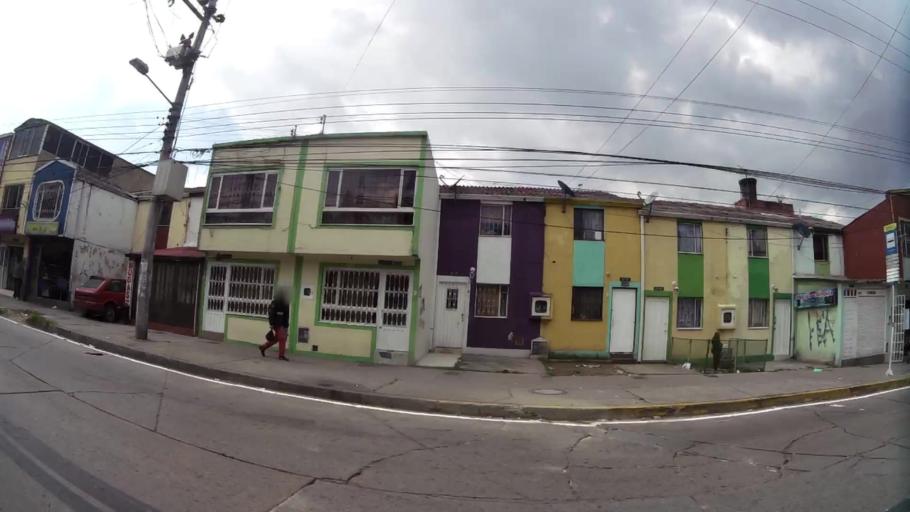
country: CO
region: Bogota D.C.
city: Bogota
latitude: 4.5621
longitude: -74.0970
